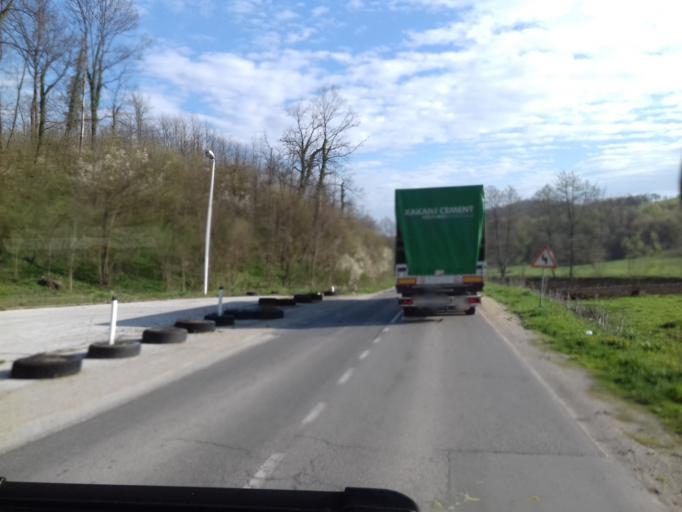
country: BA
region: Federation of Bosnia and Herzegovina
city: Tesanjka
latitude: 44.6577
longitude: 18.0165
